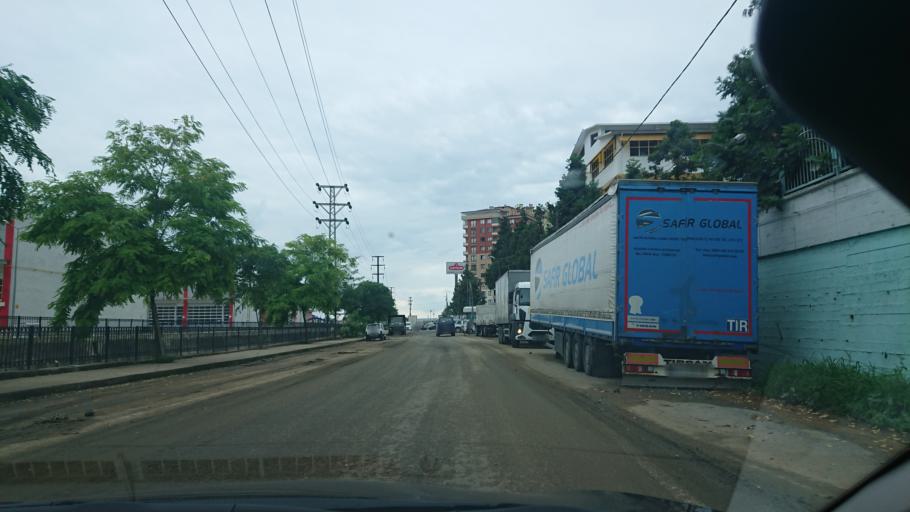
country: TR
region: Rize
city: Rize
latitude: 41.0324
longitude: 40.4824
